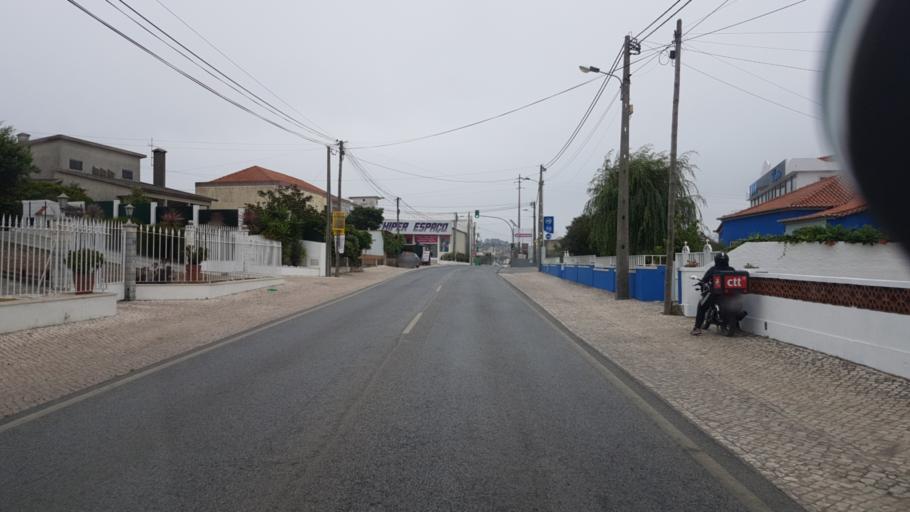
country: PT
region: Lisbon
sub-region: Torres Vedras
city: Torres Vedras
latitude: 39.0901
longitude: -9.3035
